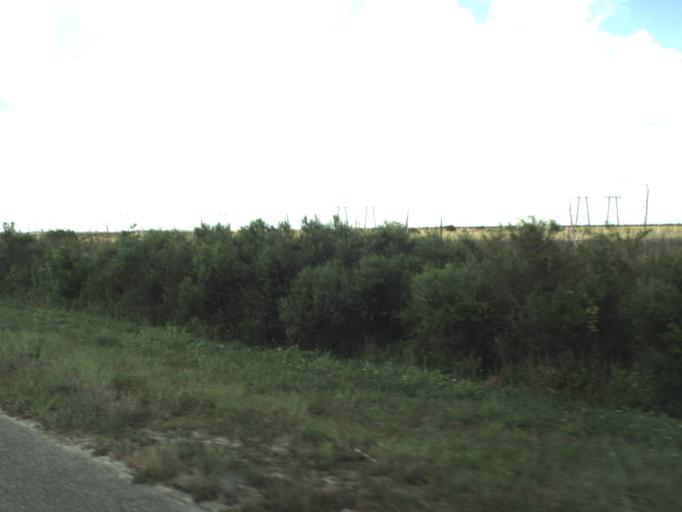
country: US
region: Florida
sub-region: Miami-Dade County
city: Palm Springs North
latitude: 25.9738
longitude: -80.4319
